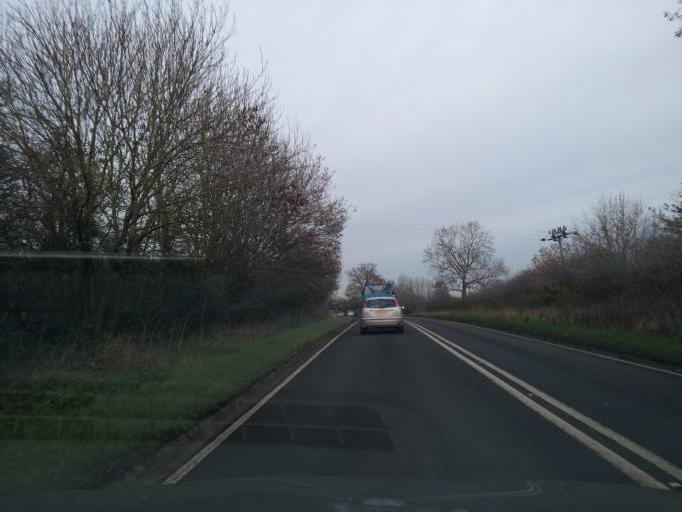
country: GB
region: England
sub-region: Buckinghamshire
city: Stewkley
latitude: 51.8662
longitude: -0.7594
